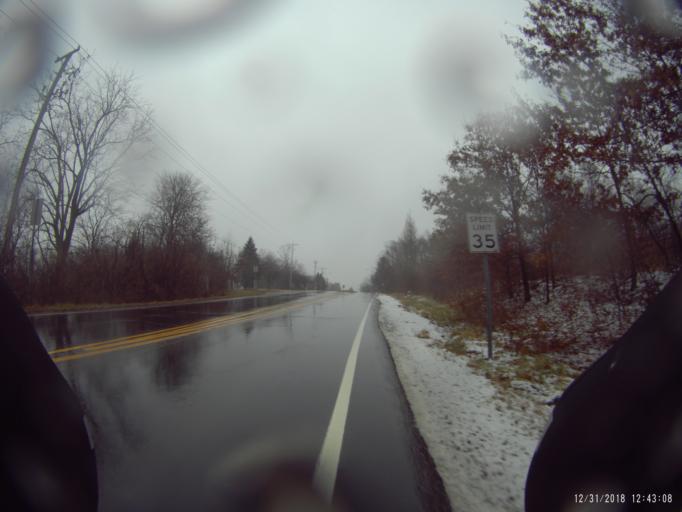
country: US
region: Wisconsin
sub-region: Dane County
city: Verona
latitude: 43.0298
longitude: -89.5098
